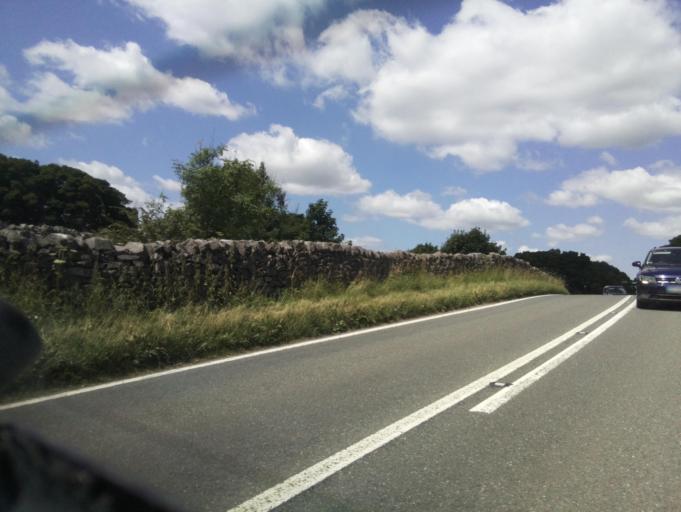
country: GB
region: England
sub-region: Derbyshire
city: Ashbourne
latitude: 53.0928
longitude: -1.7704
